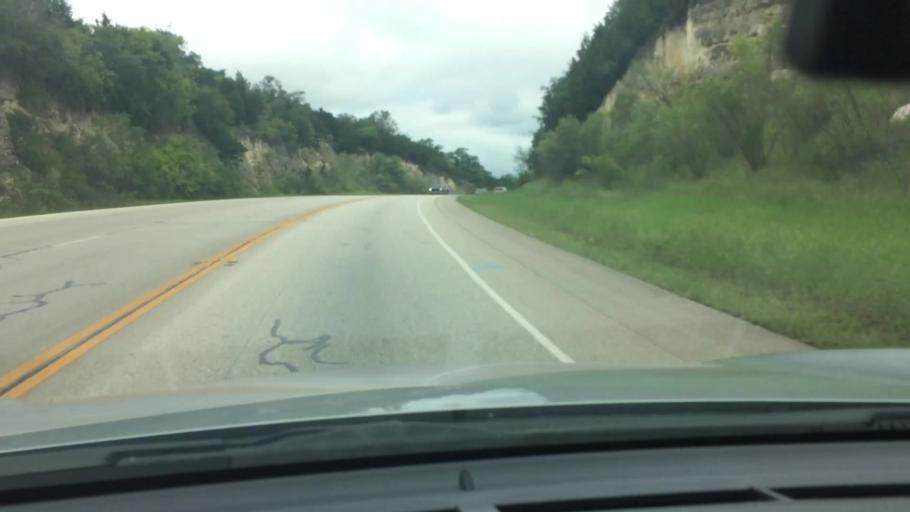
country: US
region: Texas
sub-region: Bexar County
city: Live Oak
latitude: 29.6068
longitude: -98.3683
